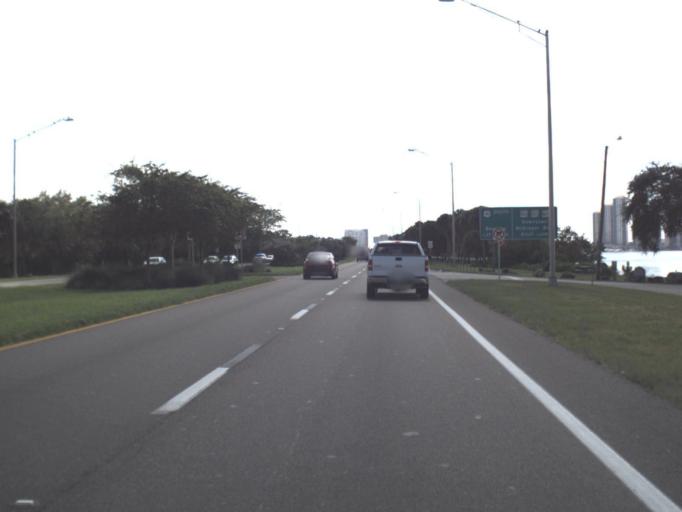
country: US
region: Florida
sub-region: Lee County
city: North Fort Myers
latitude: 26.6578
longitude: -81.8826
